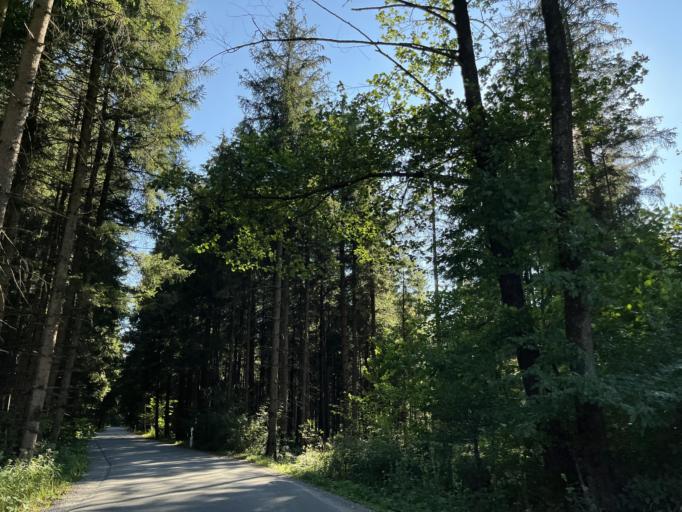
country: DE
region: Bavaria
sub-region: Upper Bavaria
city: Kolbermoor
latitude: 47.8102
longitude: 12.0724
